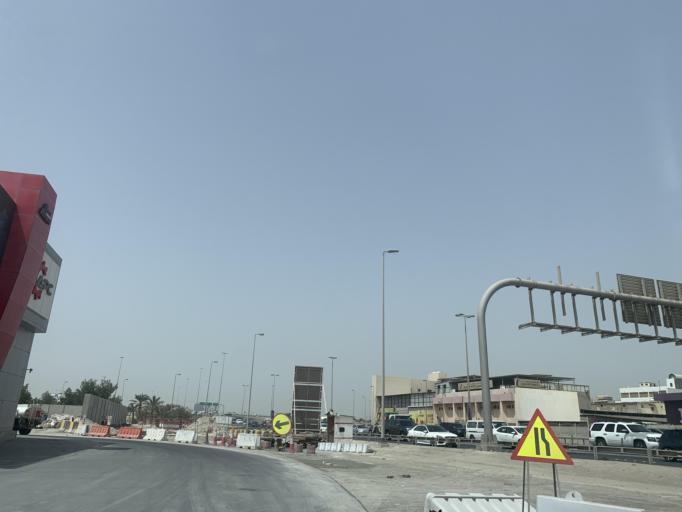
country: BH
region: Northern
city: Madinat `Isa
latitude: 26.1909
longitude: 50.5351
